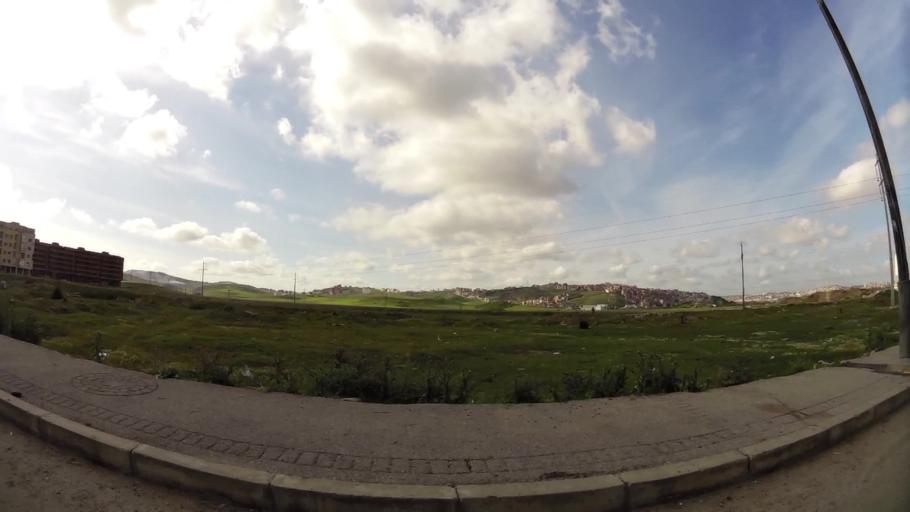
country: MA
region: Tanger-Tetouan
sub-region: Tanger-Assilah
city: Tangier
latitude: 35.7641
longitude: -5.7721
